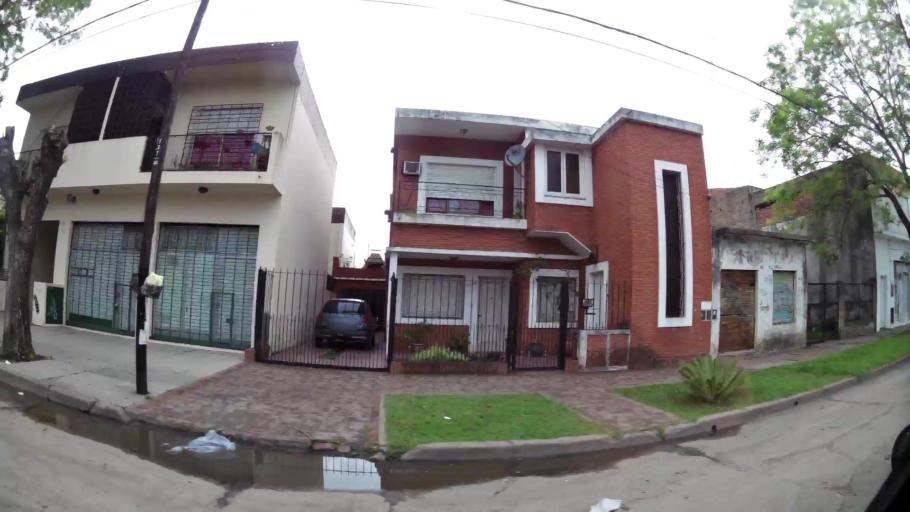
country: AR
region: Buenos Aires
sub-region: Partido de Quilmes
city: Quilmes
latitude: -34.7981
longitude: -58.2751
